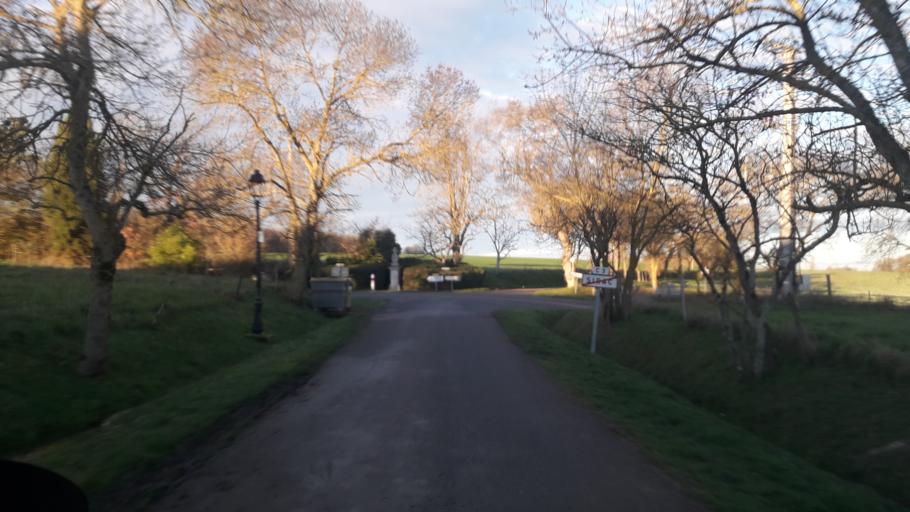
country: FR
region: Midi-Pyrenees
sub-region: Departement du Gers
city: Gimont
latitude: 43.7097
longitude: 0.9472
